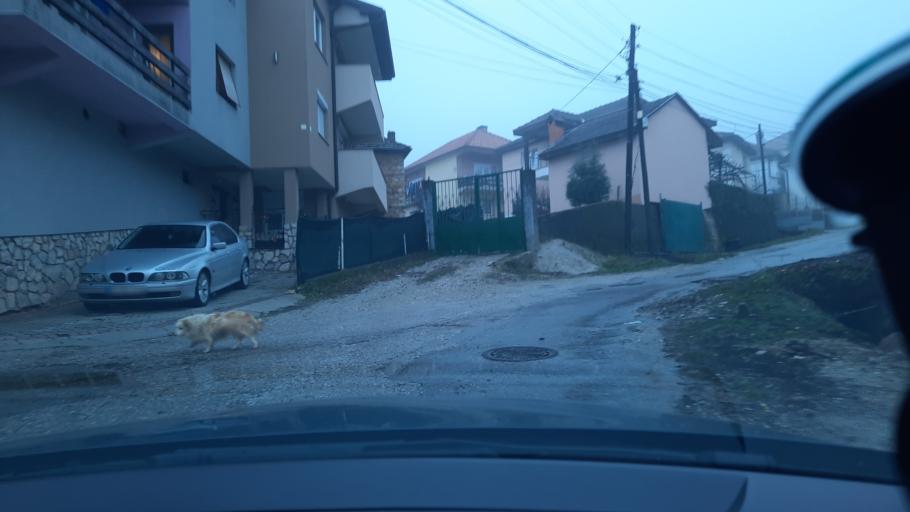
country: MK
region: Vrapciste
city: Vrapciste
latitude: 41.8382
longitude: 20.8819
